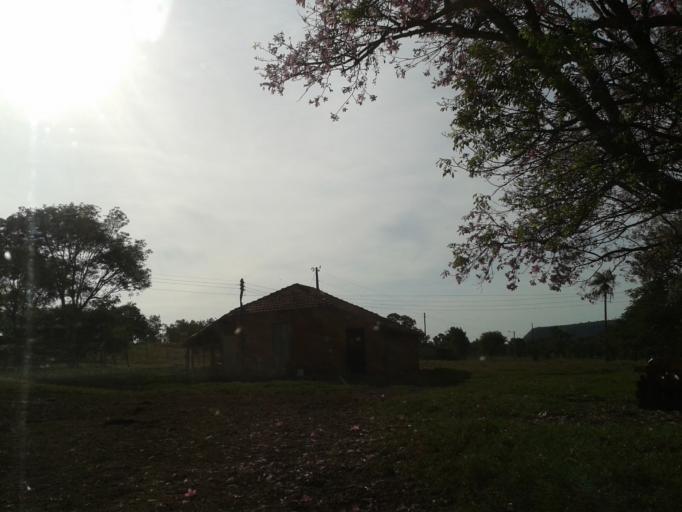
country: BR
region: Minas Gerais
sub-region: Campina Verde
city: Campina Verde
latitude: -19.5246
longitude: -49.6107
